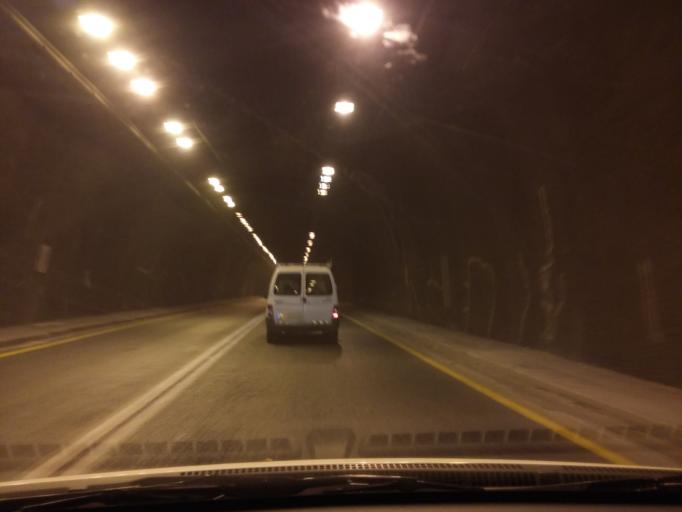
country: PS
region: West Bank
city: Bayt Jala
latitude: 31.7176
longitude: 35.1802
